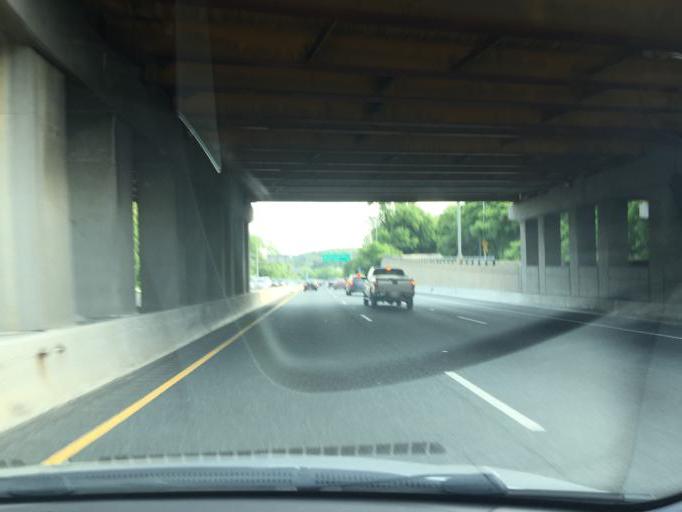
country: US
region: Maryland
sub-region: City of Baltimore
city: Baltimore
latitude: 39.3450
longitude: -76.6471
